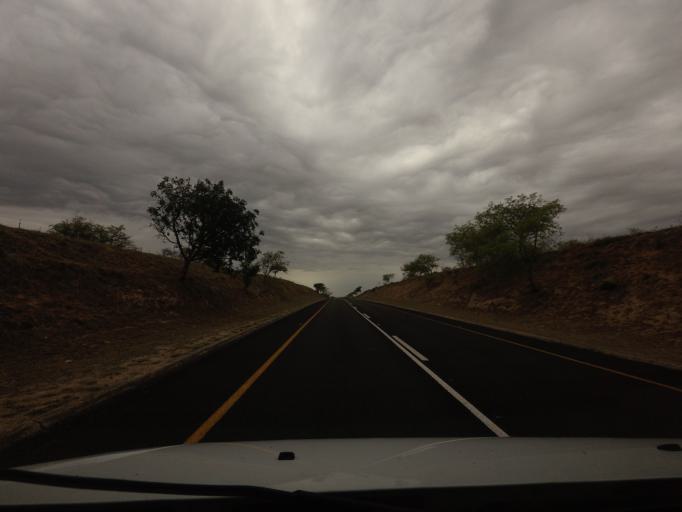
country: ZA
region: Limpopo
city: Thulamahashi
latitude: -24.5684
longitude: 31.0770
